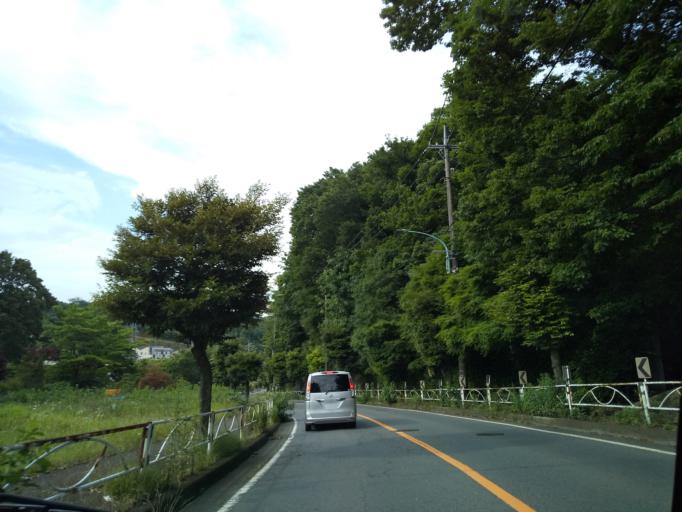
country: JP
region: Kanagawa
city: Atsugi
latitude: 35.4801
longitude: 139.3181
